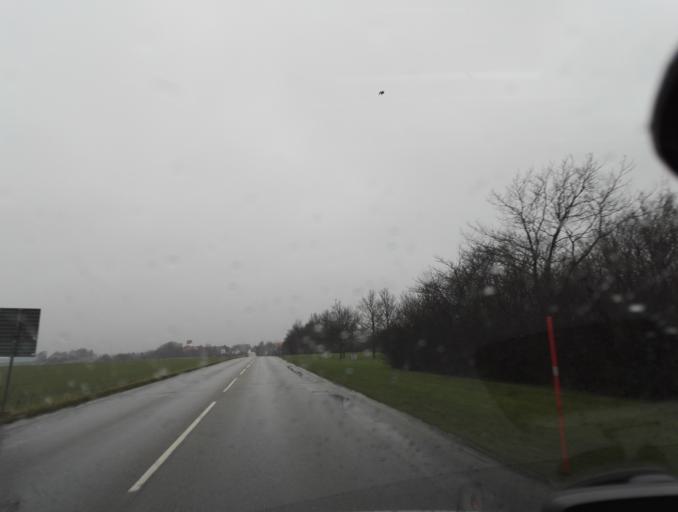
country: SE
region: Skane
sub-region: Lunds Kommun
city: Lund
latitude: 55.7350
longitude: 13.1754
